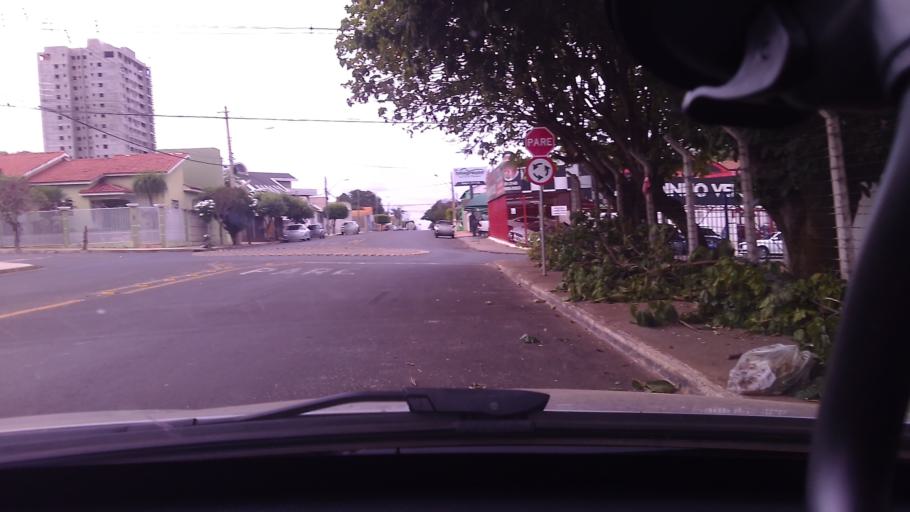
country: BR
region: Goias
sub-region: Mineiros
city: Mineiros
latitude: -17.5650
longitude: -52.5626
